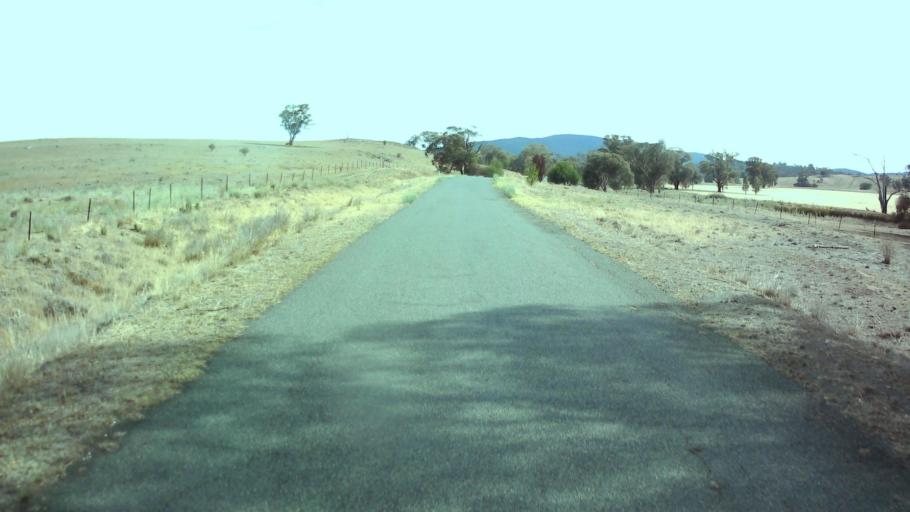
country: AU
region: New South Wales
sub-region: Weddin
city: Grenfell
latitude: -33.8210
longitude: 148.2898
